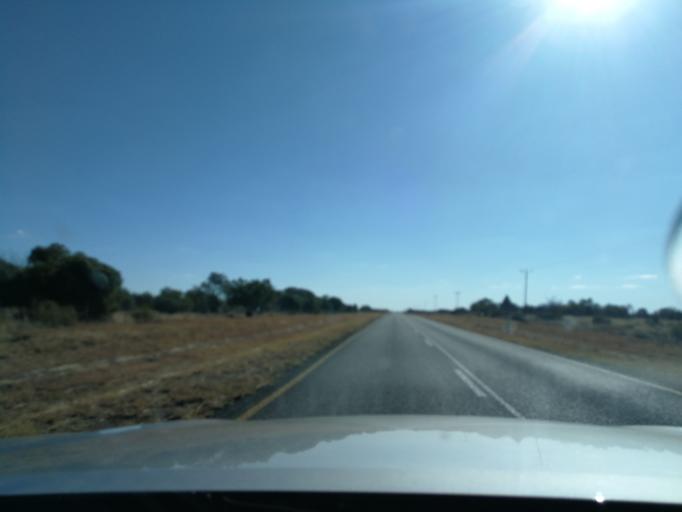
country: ZA
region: North-West
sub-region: Ngaka Modiri Molema District Municipality
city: Zeerust
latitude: -25.7682
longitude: 25.9863
